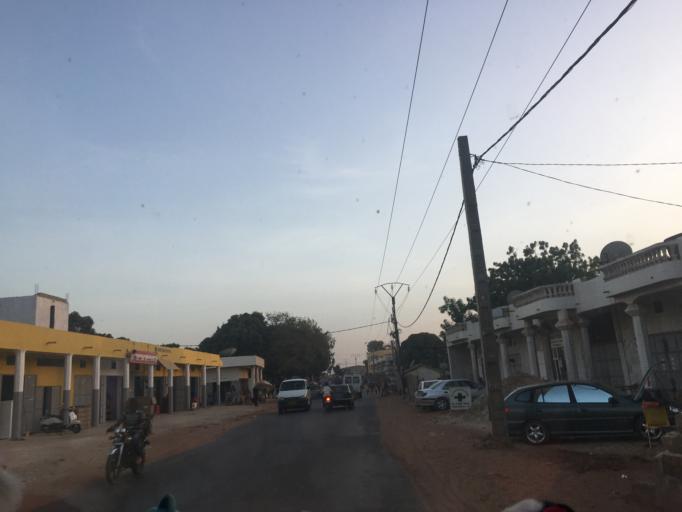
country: GM
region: Western
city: Abuko
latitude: 13.3834
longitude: -16.6791
